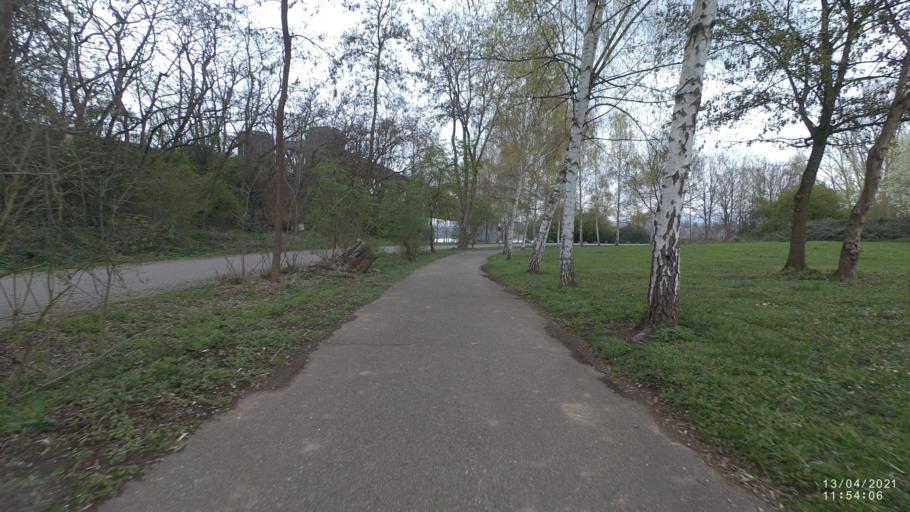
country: DE
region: Rheinland-Pfalz
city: Urmitz
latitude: 50.4187
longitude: 7.5287
